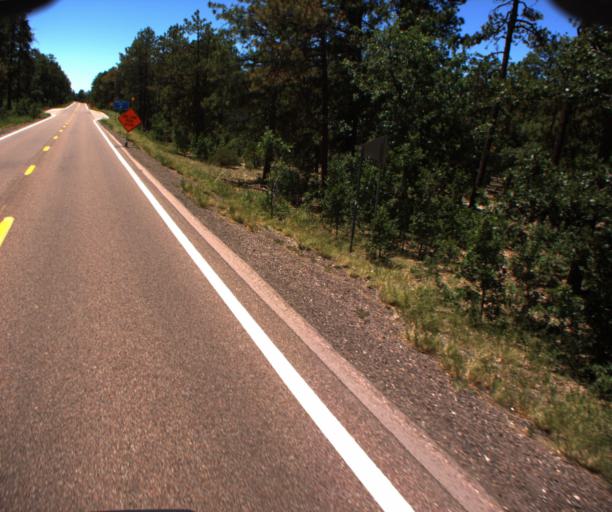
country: US
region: Arizona
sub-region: Gila County
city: Pine
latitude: 34.4377
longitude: -111.4981
